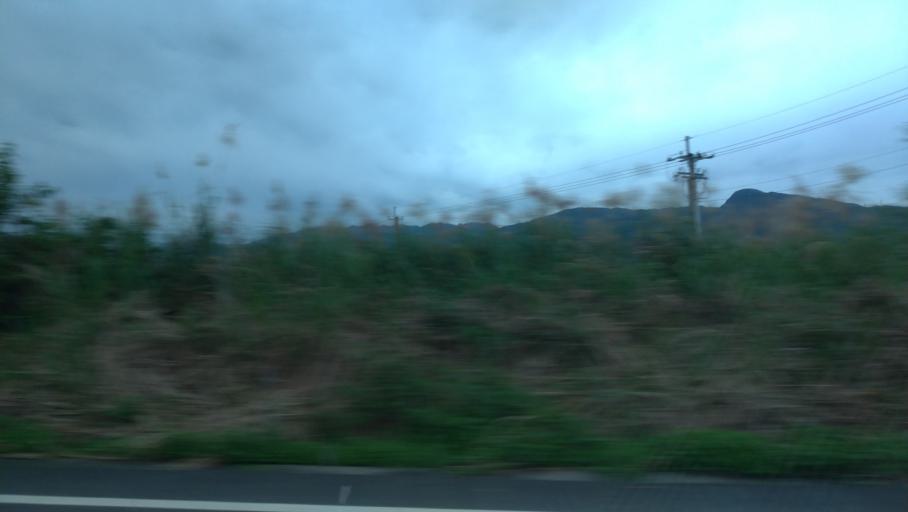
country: TW
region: Taiwan
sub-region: Yilan
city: Yilan
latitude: 24.8225
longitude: 121.7984
